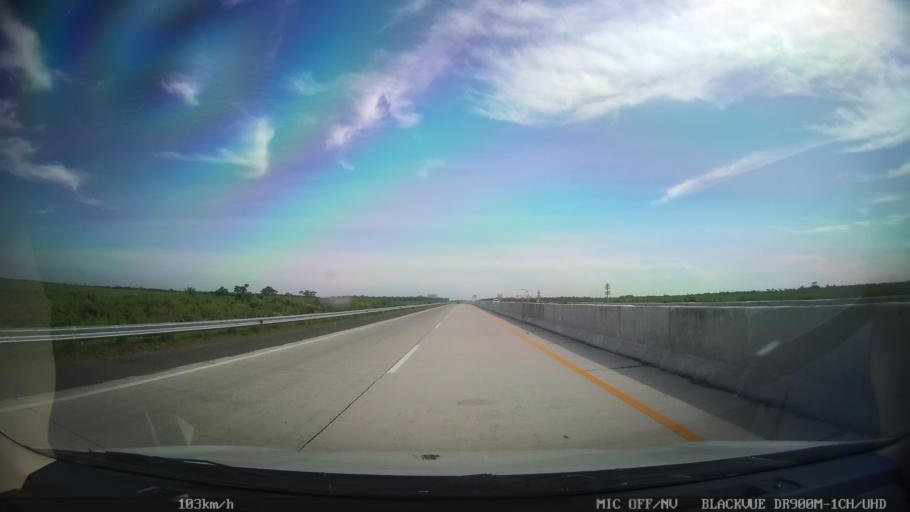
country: ID
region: North Sumatra
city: Binjai
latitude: 3.6795
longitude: 98.5369
